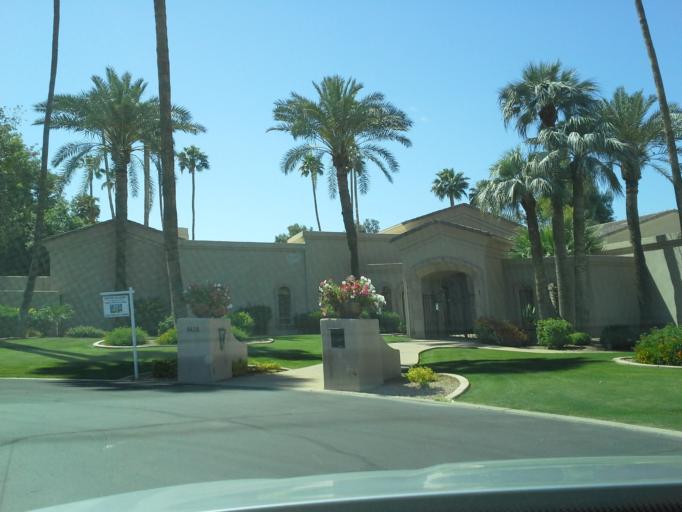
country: US
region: Arizona
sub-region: Maricopa County
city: Paradise Valley
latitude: 33.5601
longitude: -111.9319
